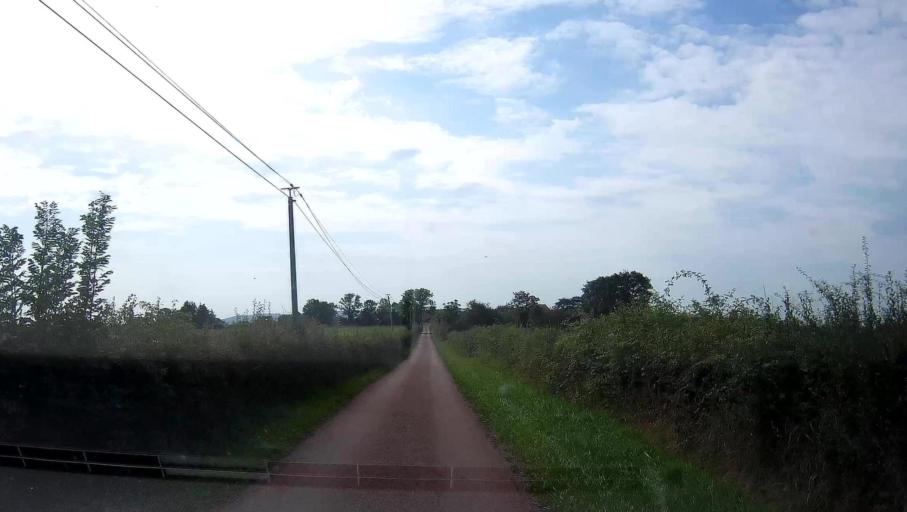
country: FR
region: Bourgogne
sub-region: Departement de Saone-et-Loire
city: Saint-Leger-sur-Dheune
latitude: 46.8959
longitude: 4.6144
